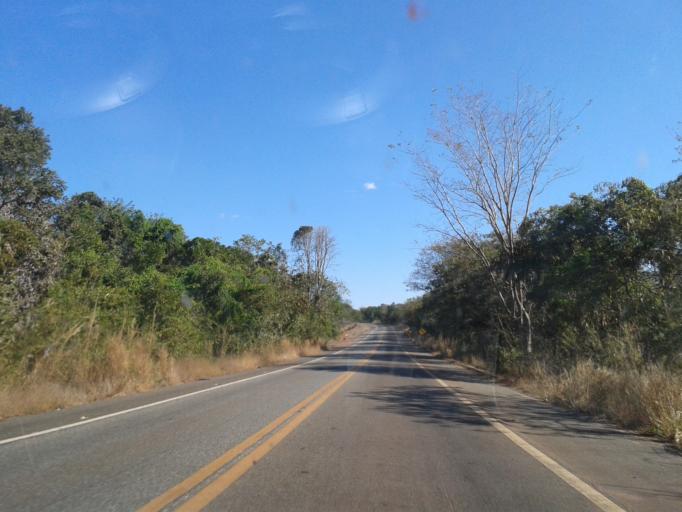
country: BR
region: Goias
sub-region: Mozarlandia
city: Mozarlandia
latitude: -14.8309
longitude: -50.5359
